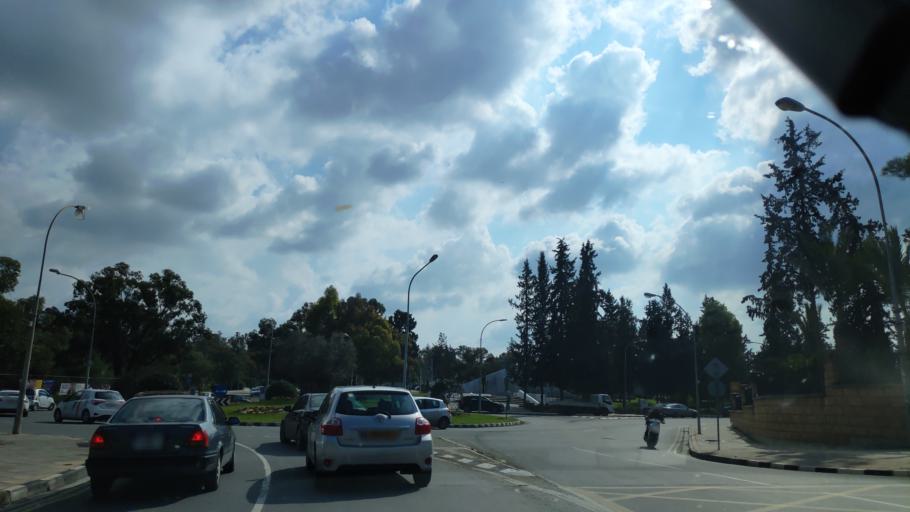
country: CY
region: Lefkosia
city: Nicosia
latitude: 35.1552
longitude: 33.3495
